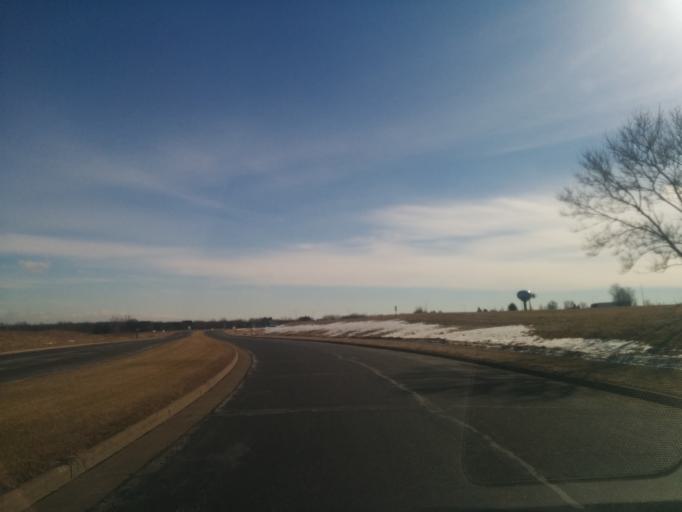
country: US
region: Wisconsin
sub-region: Kenosha County
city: Pleasant Prairie
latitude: 42.5267
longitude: -87.9510
